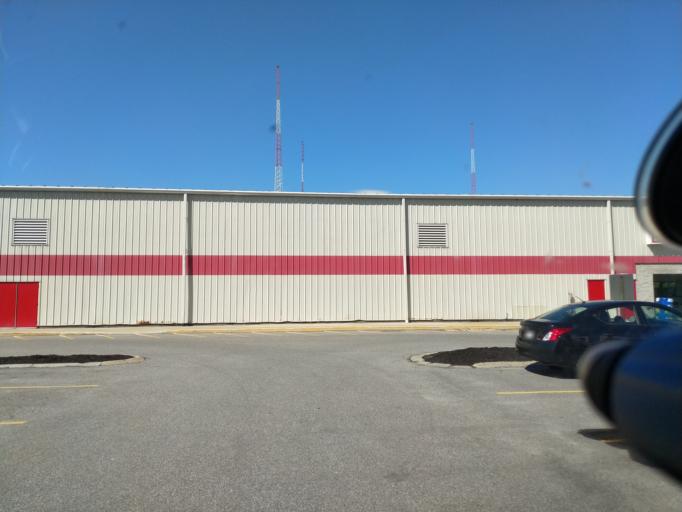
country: US
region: Maine
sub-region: Cumberland County
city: South Portland Gardens
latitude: 43.6880
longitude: -70.3195
